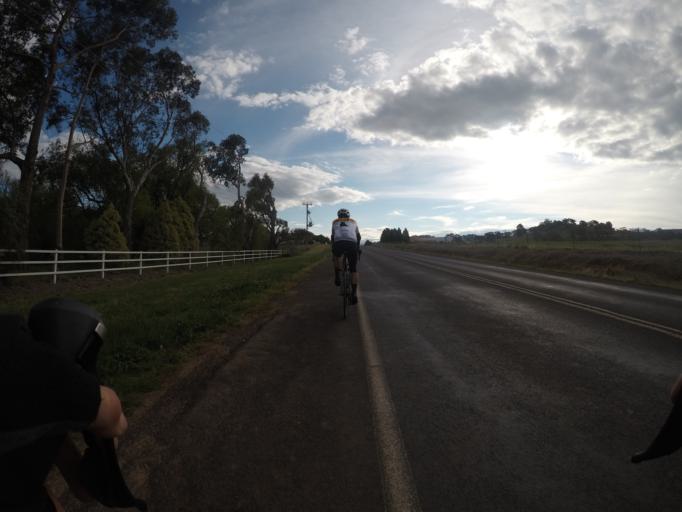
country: AU
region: New South Wales
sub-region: Orange Municipality
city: Orange
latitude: -33.2965
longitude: 148.9999
